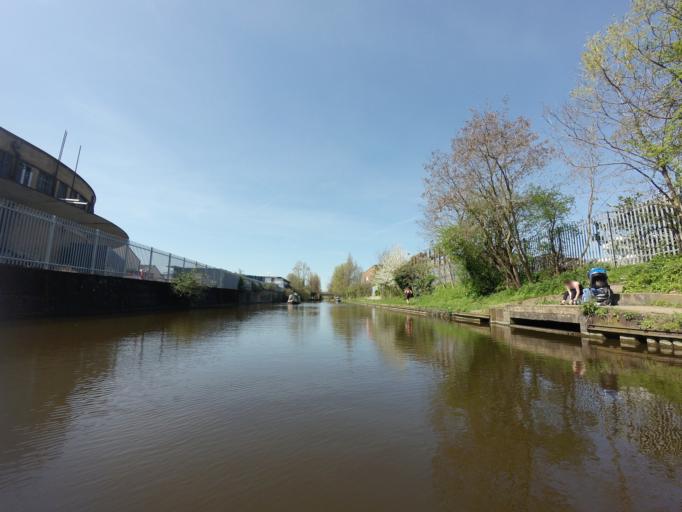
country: GB
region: England
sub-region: Greater London
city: Hayes
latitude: 51.5062
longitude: -0.4235
